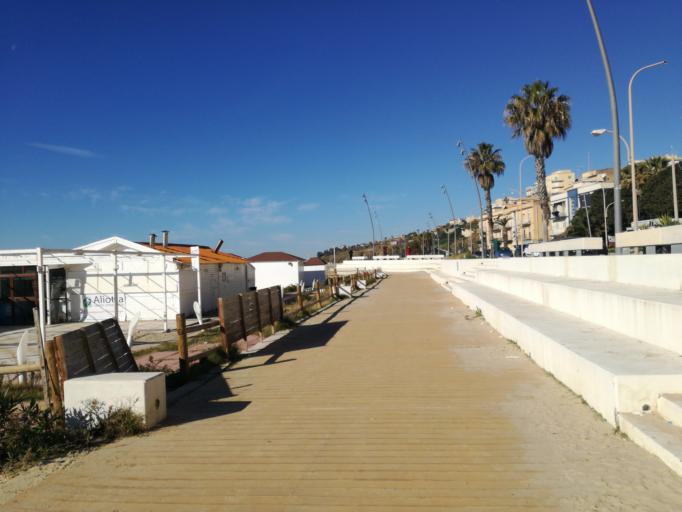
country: IT
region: Sicily
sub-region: Provincia di Caltanissetta
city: Gela
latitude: 37.0655
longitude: 14.2443
